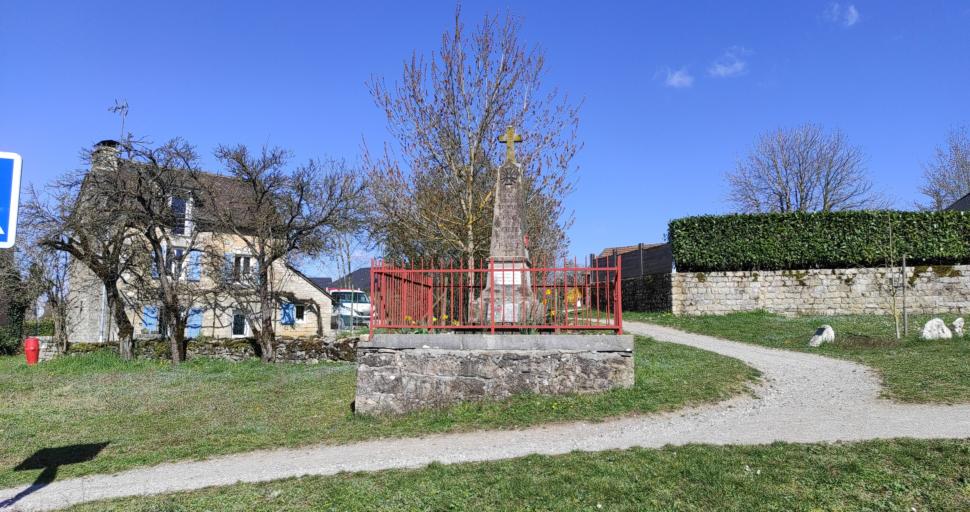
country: FR
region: Midi-Pyrenees
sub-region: Departement de l'Aveyron
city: Sebazac-Concoures
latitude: 44.4447
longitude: 2.6497
